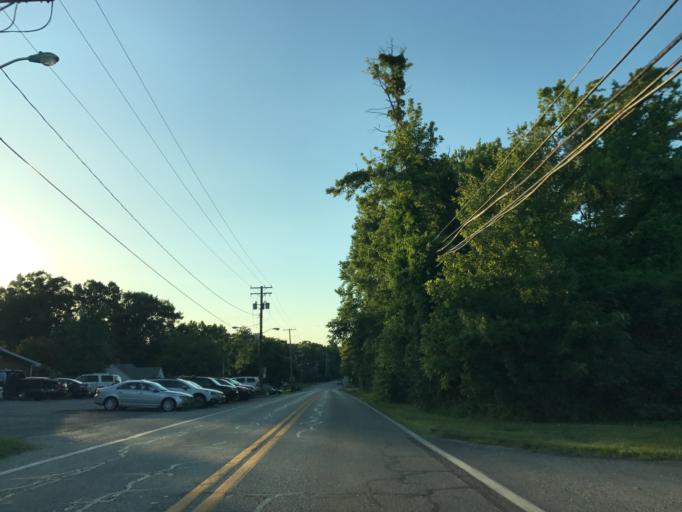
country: US
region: Maryland
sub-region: Anne Arundel County
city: Mayo
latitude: 38.8961
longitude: -76.5121
